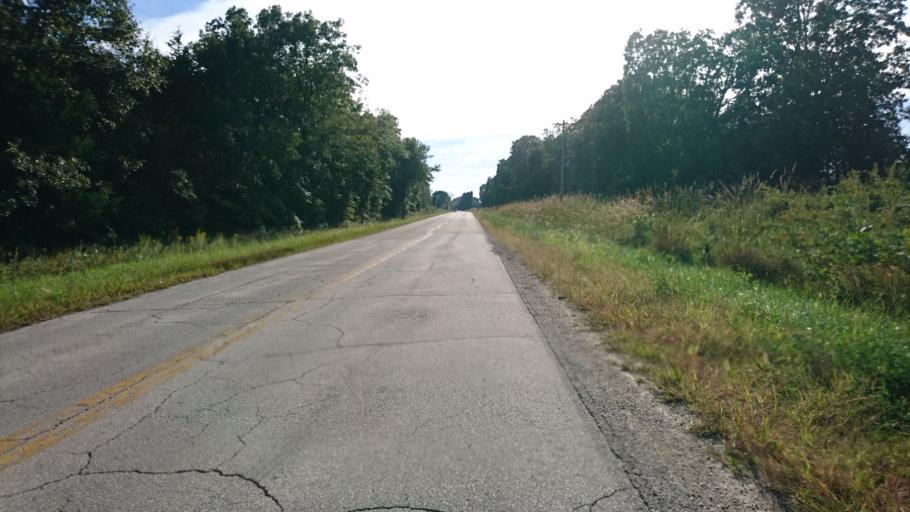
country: US
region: Missouri
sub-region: Crawford County
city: Cuba
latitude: 38.1074
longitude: -91.3406
